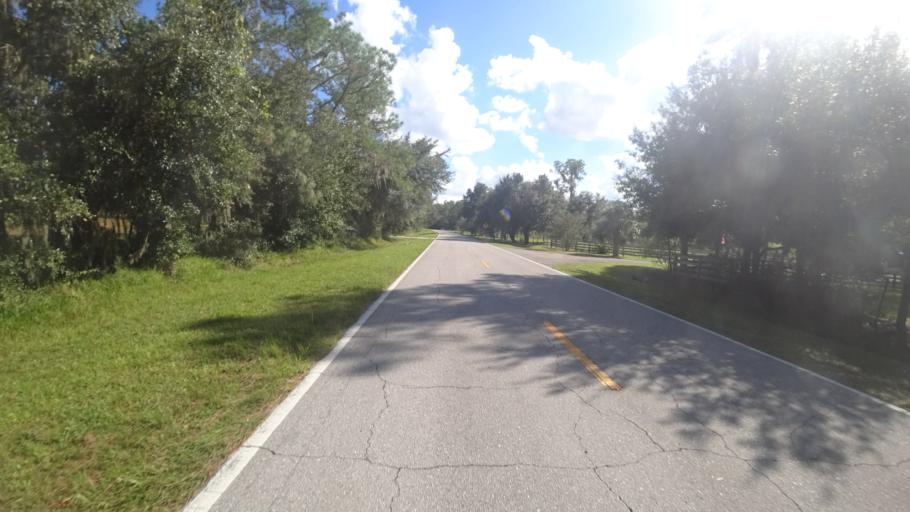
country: US
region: Florida
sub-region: Hardee County
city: Wauchula
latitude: 27.4728
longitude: -82.0788
